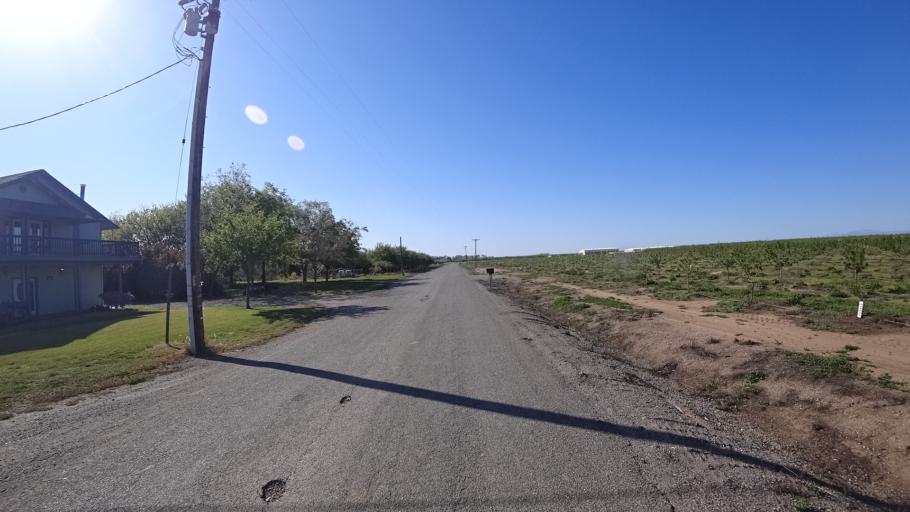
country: US
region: California
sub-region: Glenn County
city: Hamilton City
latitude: 39.7702
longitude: -122.0477
